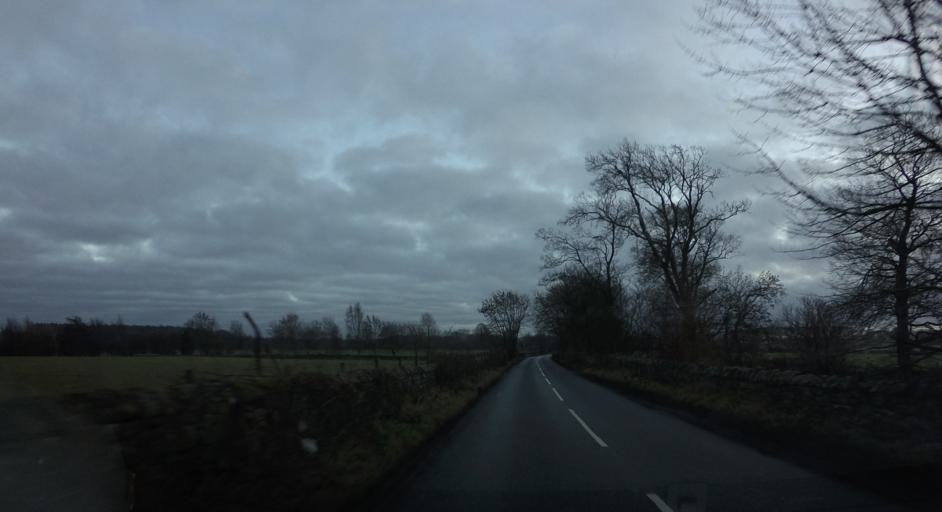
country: GB
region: Scotland
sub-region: Fife
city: Crossford
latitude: 56.0573
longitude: -3.4924
